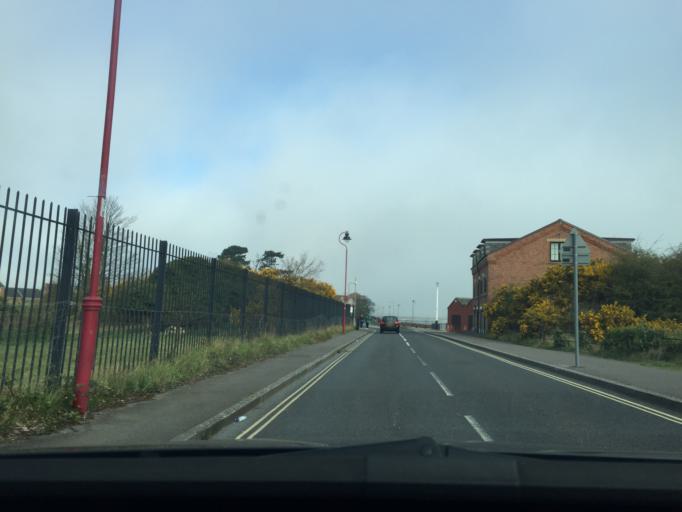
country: GB
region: England
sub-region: Hampshire
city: Gosport
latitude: 50.8079
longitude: -1.1274
